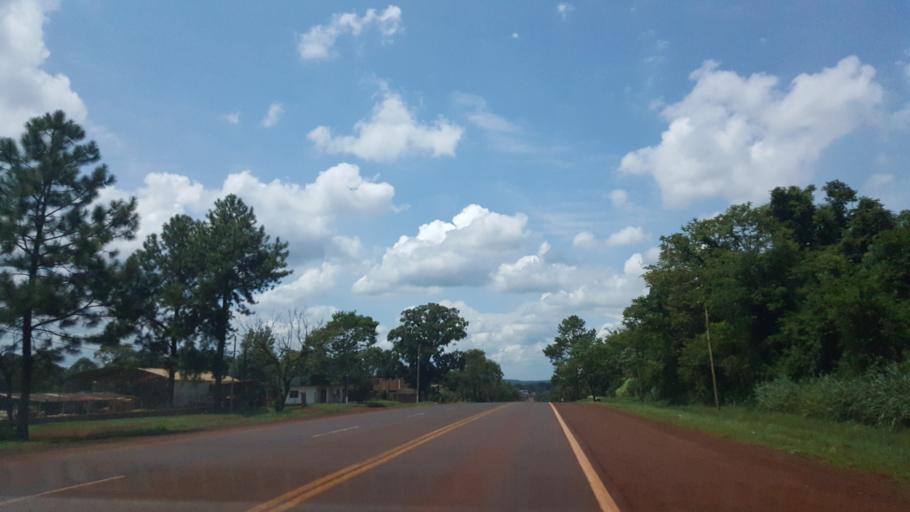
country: AR
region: Misiones
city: Garuhape
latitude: -26.8216
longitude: -54.9699
